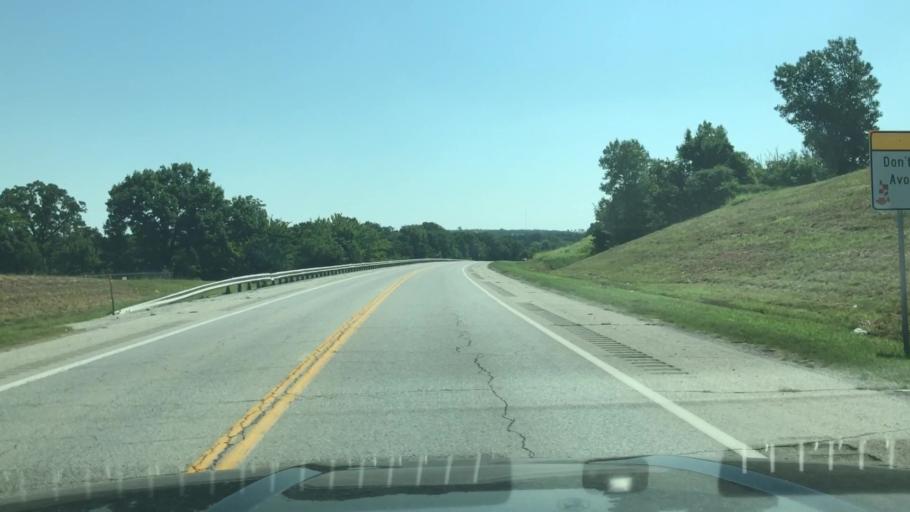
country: US
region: Oklahoma
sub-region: Creek County
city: Drumright
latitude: 35.9881
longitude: -96.5759
